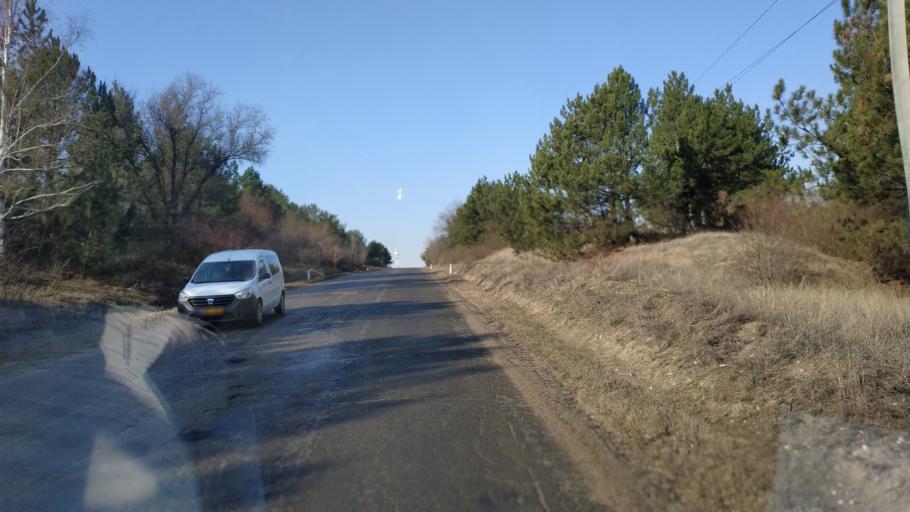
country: MD
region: Chisinau
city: Singera
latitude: 46.6972
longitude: 29.0621
